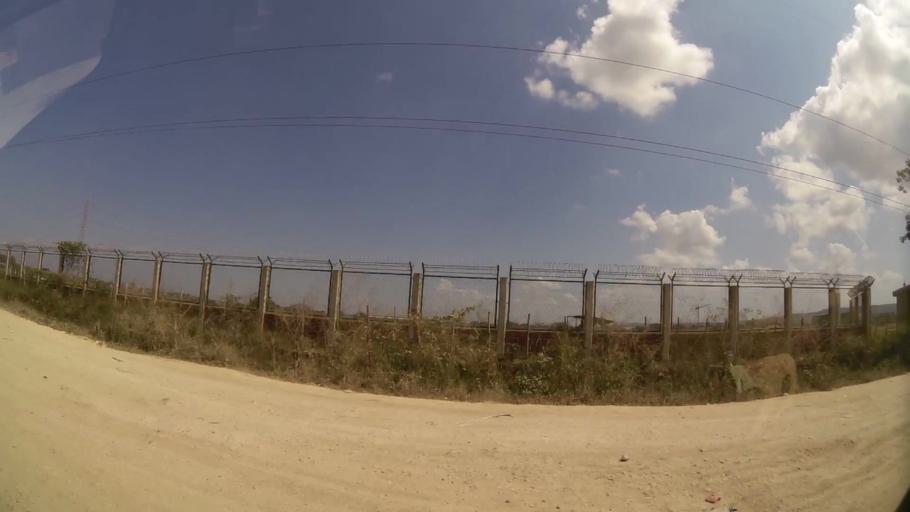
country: CO
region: Bolivar
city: Cartagena
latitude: 10.3480
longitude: -75.4880
